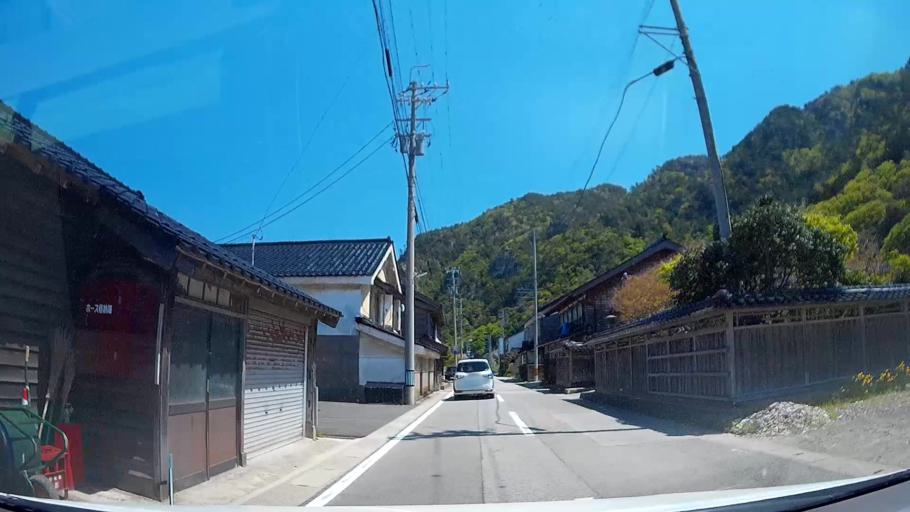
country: JP
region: Ishikawa
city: Nanao
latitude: 37.4598
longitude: 137.0778
